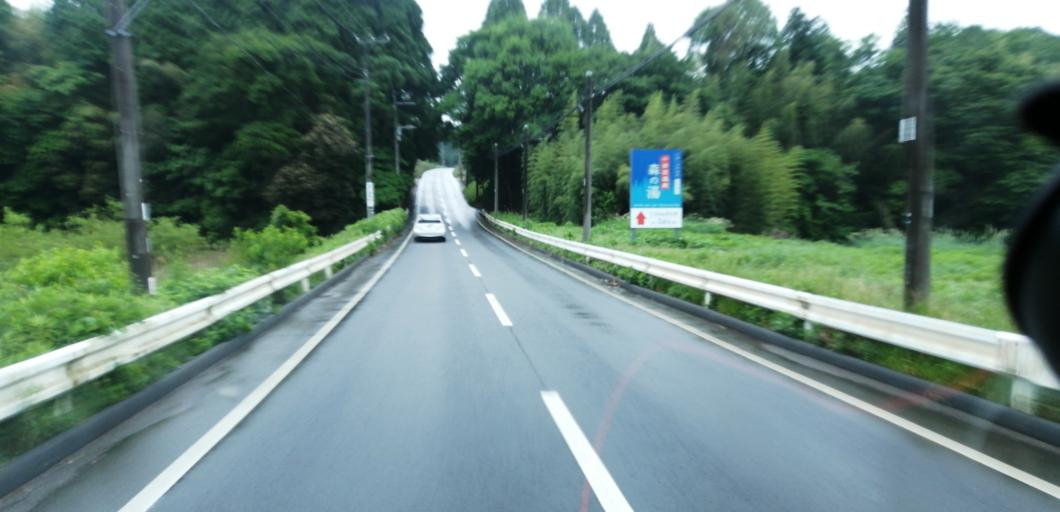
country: JP
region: Chiba
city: Yachimata
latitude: 35.6174
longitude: 140.2885
